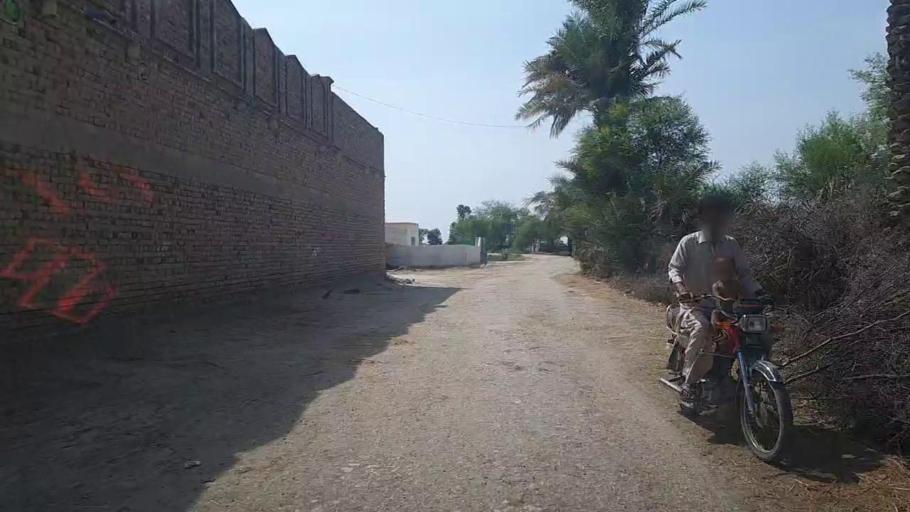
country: PK
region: Sindh
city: Ubauro
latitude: 28.1338
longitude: 69.8342
